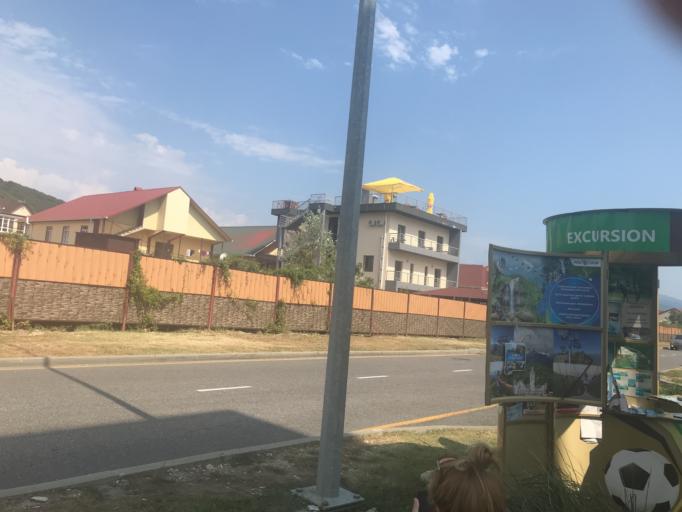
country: RU
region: Krasnodarskiy
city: Vysokoye
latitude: 43.4039
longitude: 39.9840
